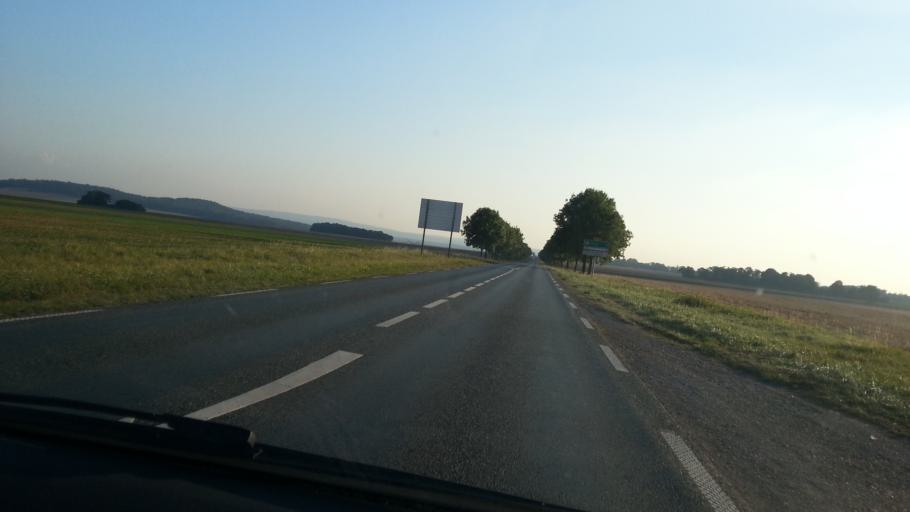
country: FR
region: Picardie
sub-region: Departement de l'Oise
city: Estrees-Saint-Denis
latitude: 49.4014
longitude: 2.6257
